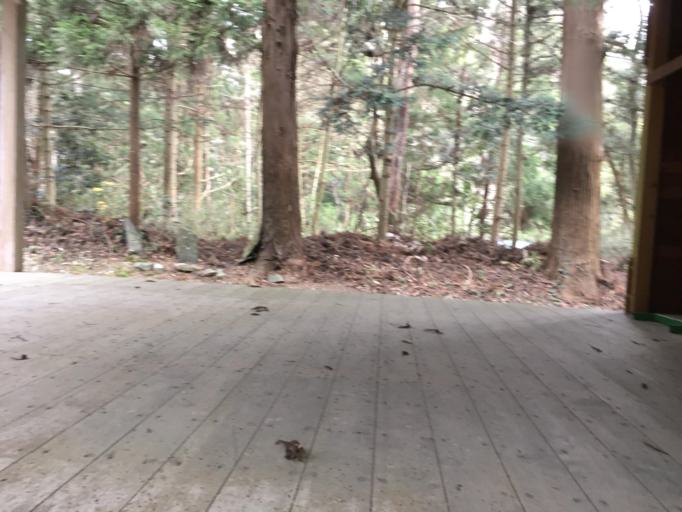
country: JP
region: Miyagi
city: Wakuya
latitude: 38.6820
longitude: 141.2770
